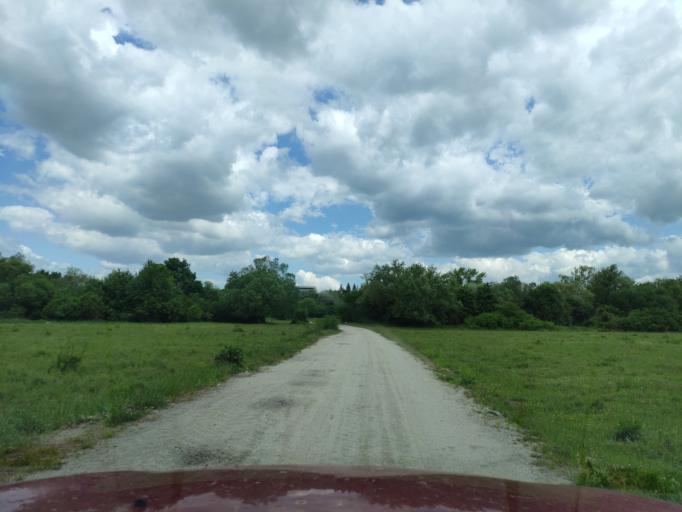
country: SK
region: Kosicky
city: Kosice
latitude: 48.8410
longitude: 21.3209
